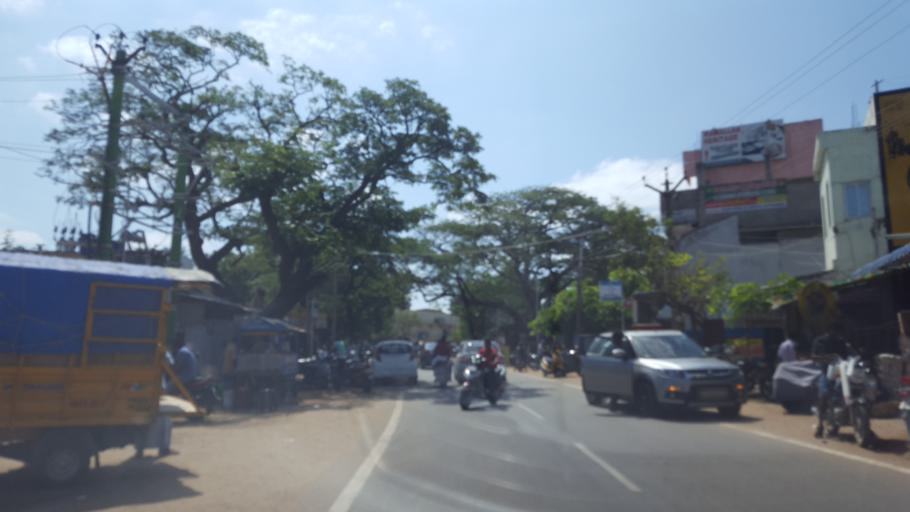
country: IN
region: Tamil Nadu
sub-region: Kancheepuram
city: Mamallapuram
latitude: 12.6226
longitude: 80.1942
